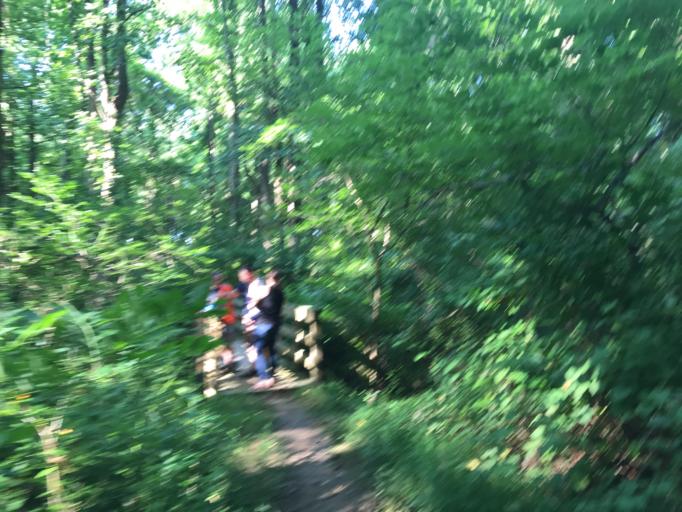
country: US
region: Delaware
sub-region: New Castle County
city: Newark
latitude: 39.7214
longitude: -75.7784
